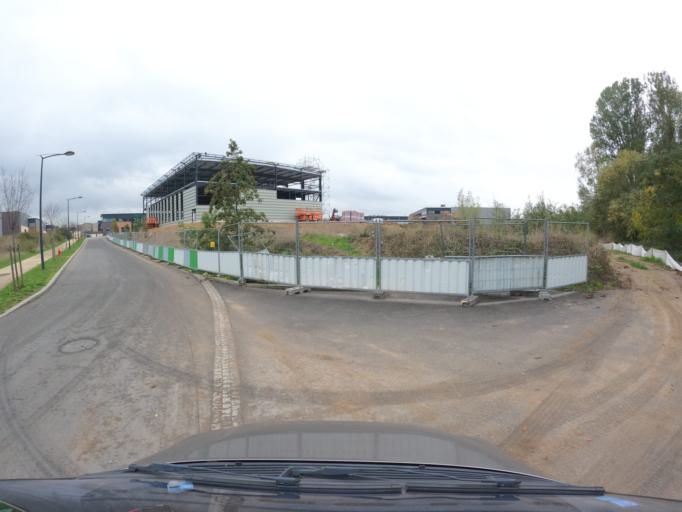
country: FR
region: Ile-de-France
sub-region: Departement du Val-de-Marne
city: Bonneuil-sur-Marne
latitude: 48.7684
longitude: 2.4993
